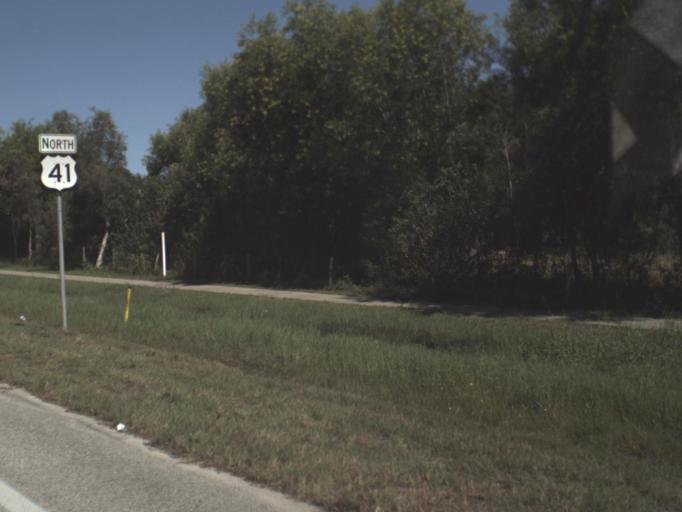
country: US
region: Florida
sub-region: Lee County
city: Estero
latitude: 26.4209
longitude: -81.8114
